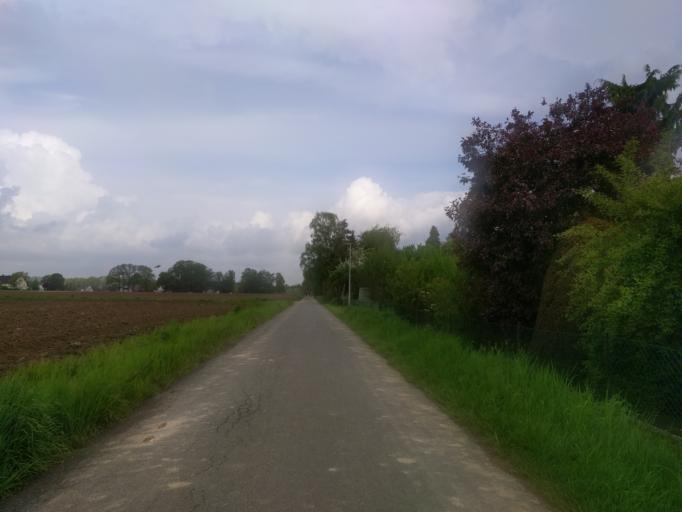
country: DE
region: North Rhine-Westphalia
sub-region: Regierungsbezirk Detmold
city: Bielefeld
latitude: 52.0551
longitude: 8.5033
